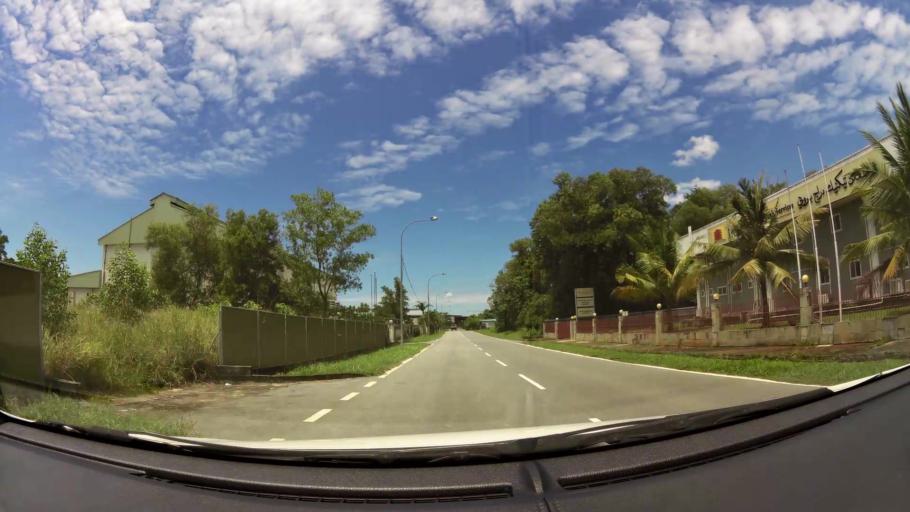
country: BN
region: Brunei and Muara
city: Bandar Seri Begawan
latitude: 5.0025
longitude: 115.0293
